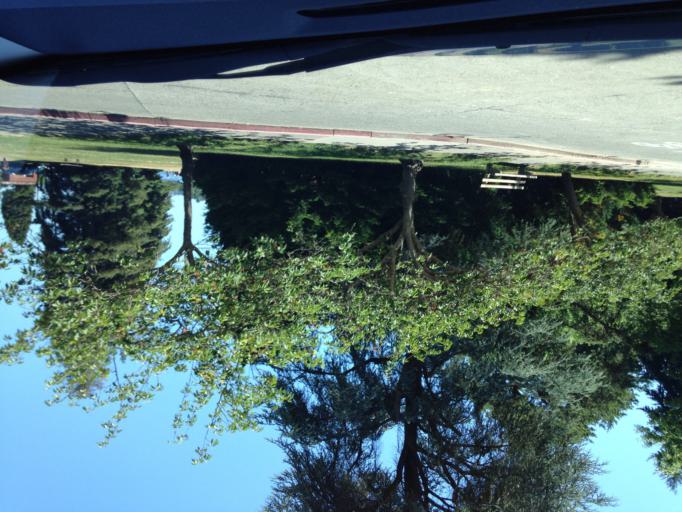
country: US
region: Washington
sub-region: King County
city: Mercer Island
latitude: 47.5498
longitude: -122.2568
